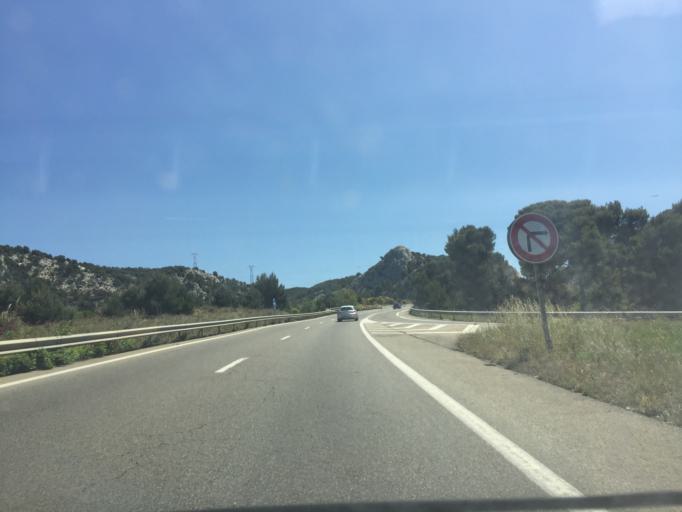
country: FR
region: Provence-Alpes-Cote d'Azur
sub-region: Departement des Bouches-du-Rhone
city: Les Pennes-Mirabeau
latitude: 43.4036
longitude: 5.2973
